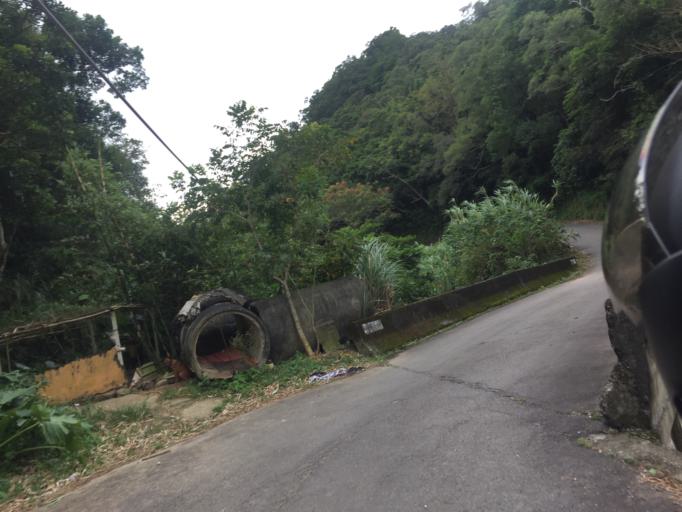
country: TW
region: Taiwan
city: Daxi
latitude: 24.7898
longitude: 121.1640
